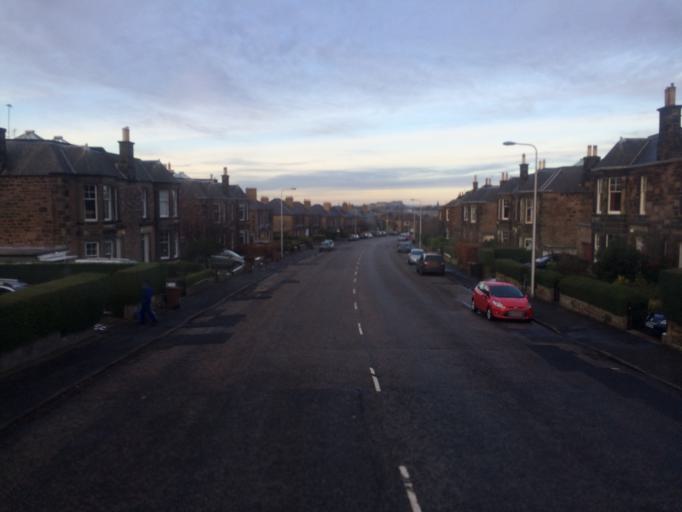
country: GB
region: Scotland
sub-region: Edinburgh
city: Colinton
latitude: 55.9167
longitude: -3.2170
